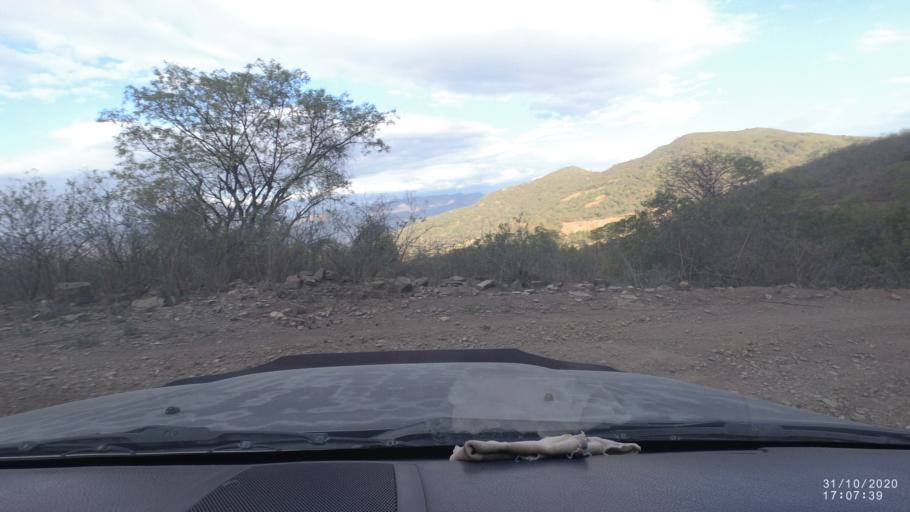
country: BO
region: Chuquisaca
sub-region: Provincia Zudanez
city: Mojocoya
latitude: -18.5450
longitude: -64.5430
